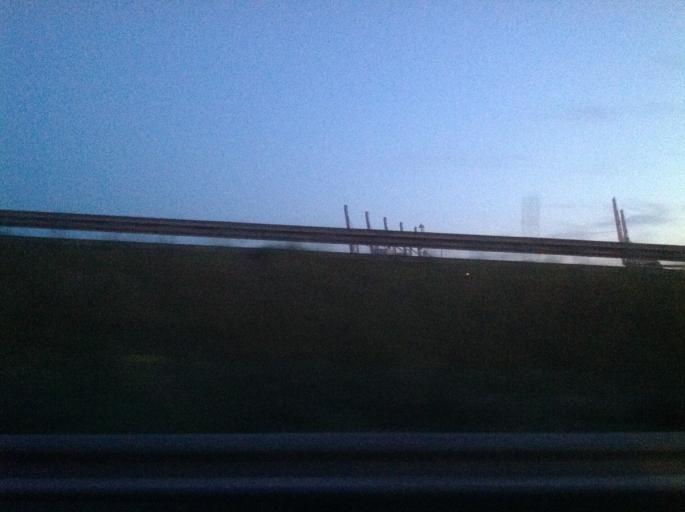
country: IT
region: Apulia
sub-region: Provincia di Taranto
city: Statte
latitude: 40.5094
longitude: 17.1625
